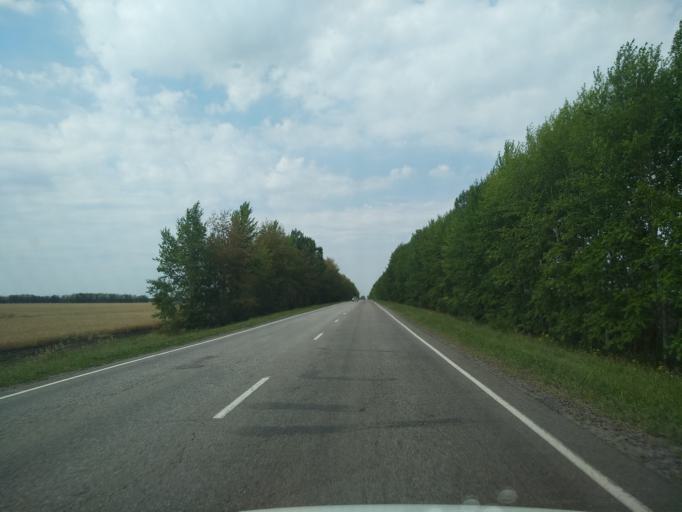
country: RU
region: Voronezj
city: Pereleshino
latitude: 51.7214
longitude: 40.0313
